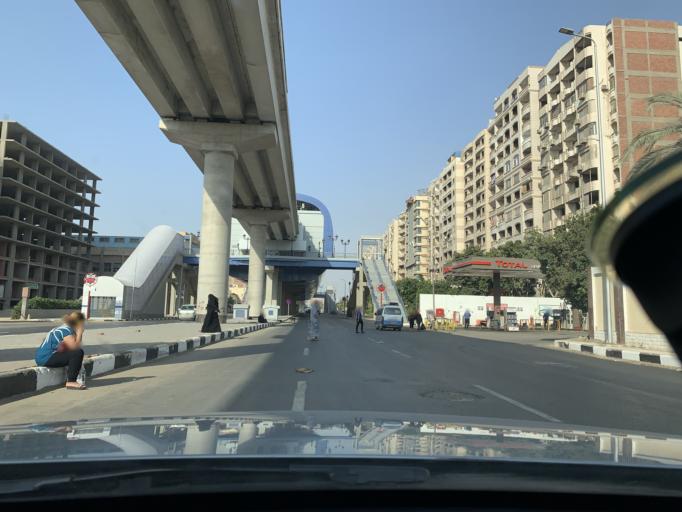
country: EG
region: Muhafazat al Qalyubiyah
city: Al Khankah
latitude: 30.1303
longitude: 31.3713
